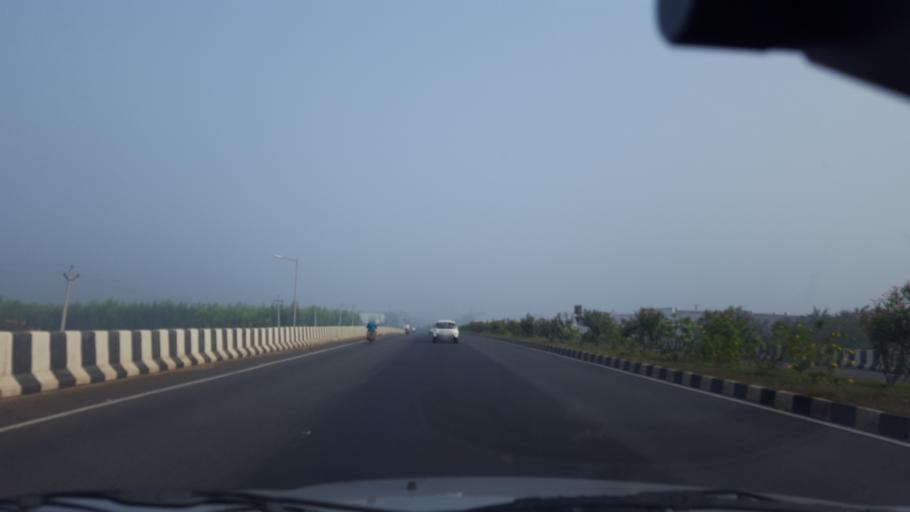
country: IN
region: Andhra Pradesh
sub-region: Prakasam
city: Ongole
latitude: 15.3909
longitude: 80.0393
